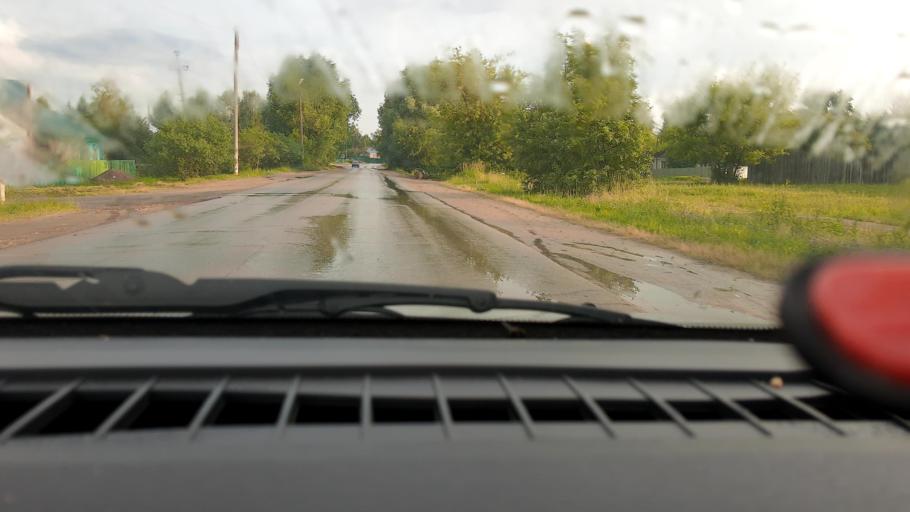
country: RU
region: Nizjnij Novgorod
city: Lukoyanov
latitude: 55.0397
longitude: 44.4963
